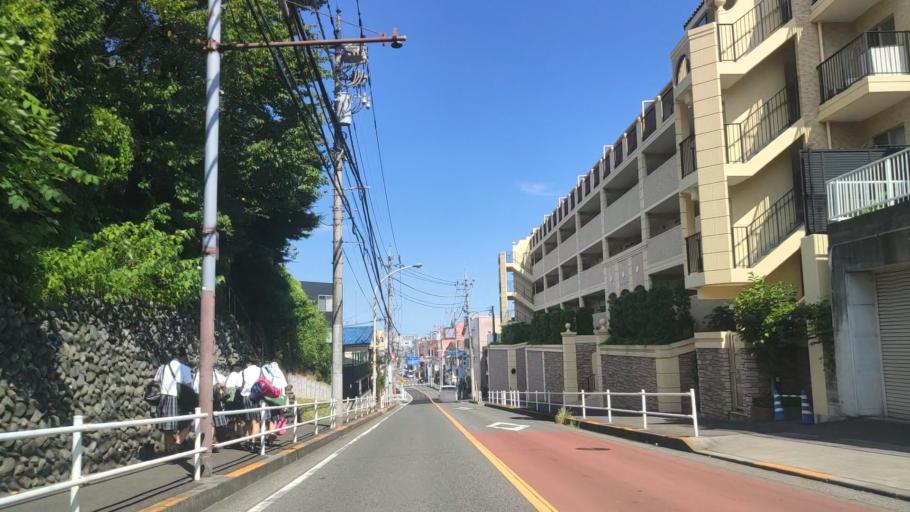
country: JP
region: Tokyo
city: Hachioji
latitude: 35.6523
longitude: 139.3314
